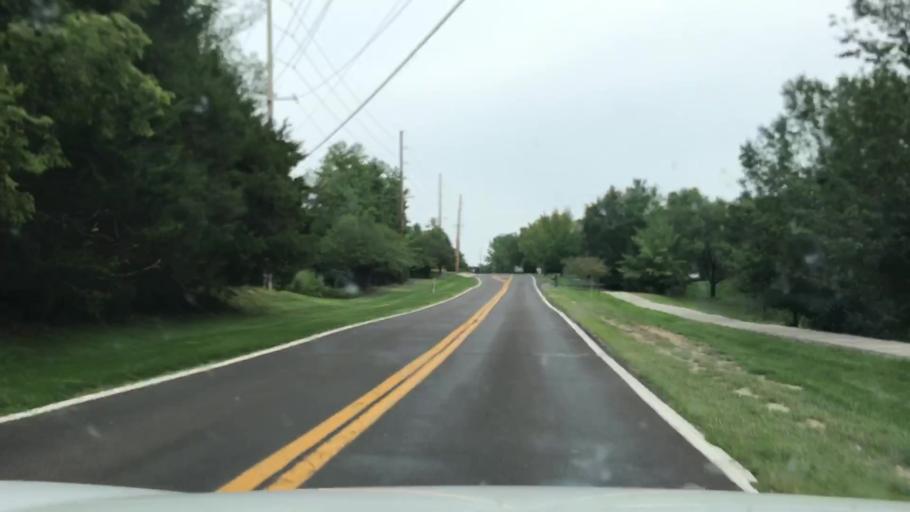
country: US
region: Missouri
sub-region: Saint Louis County
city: Clarkson Valley
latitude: 38.6335
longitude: -90.6029
